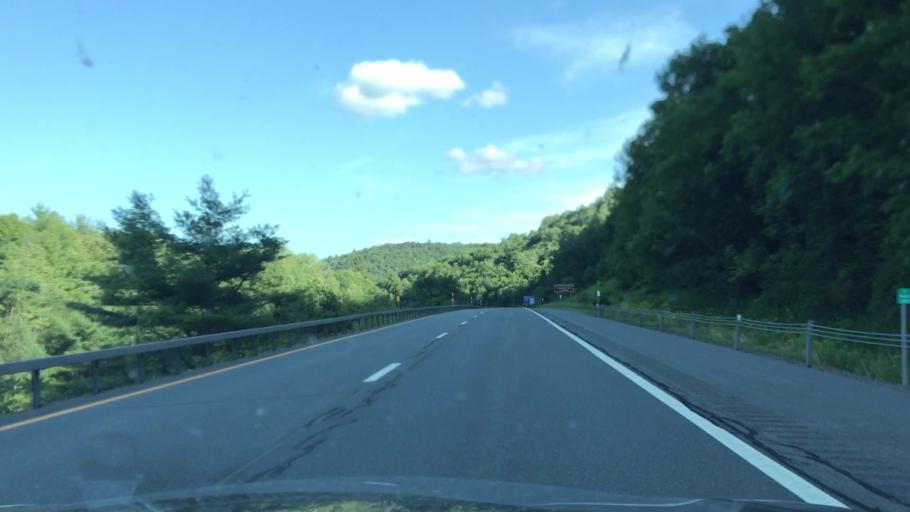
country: US
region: New York
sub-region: Sullivan County
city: Livingston Manor
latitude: 41.9417
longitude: -74.9298
